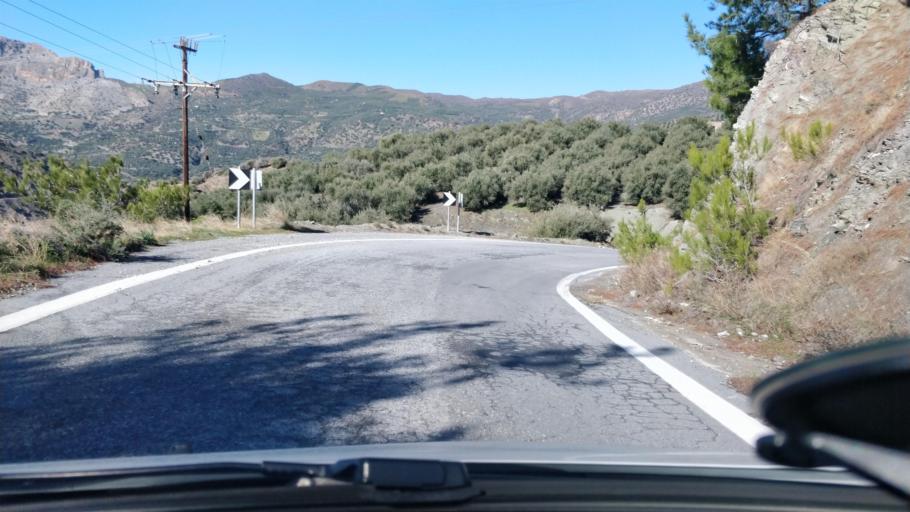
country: GR
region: Crete
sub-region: Nomos Irakleiou
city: Arkalochori
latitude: 35.0057
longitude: 25.4383
